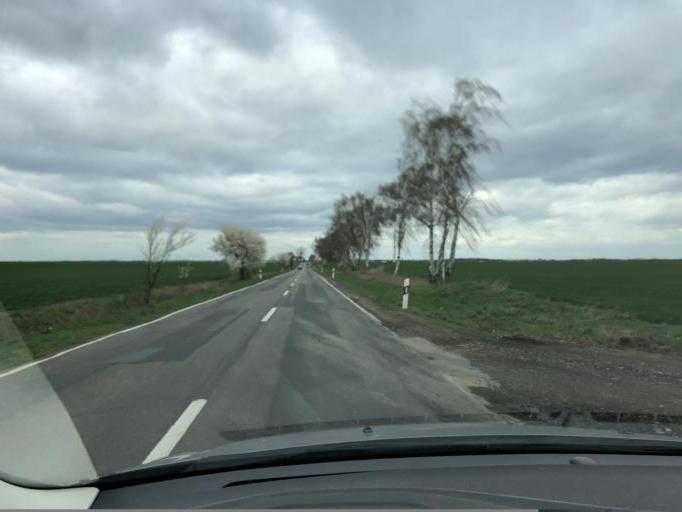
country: DE
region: Saxony-Anhalt
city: Lutzen
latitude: 51.2222
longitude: 12.1400
